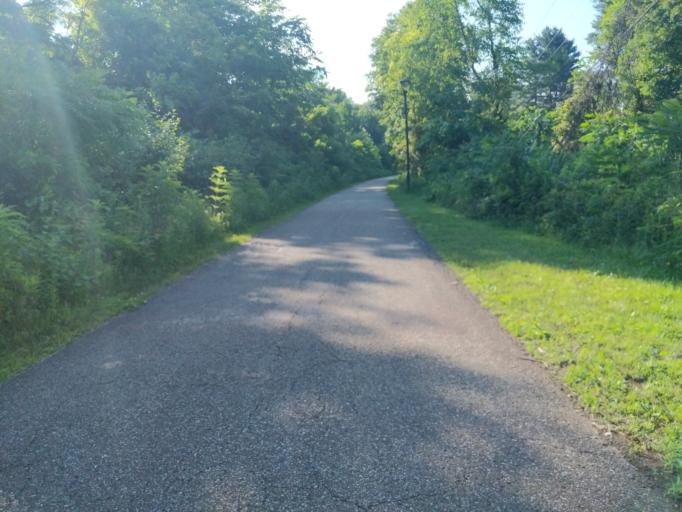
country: US
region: Ohio
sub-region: Athens County
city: Nelsonville
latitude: 39.4334
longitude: -82.2134
